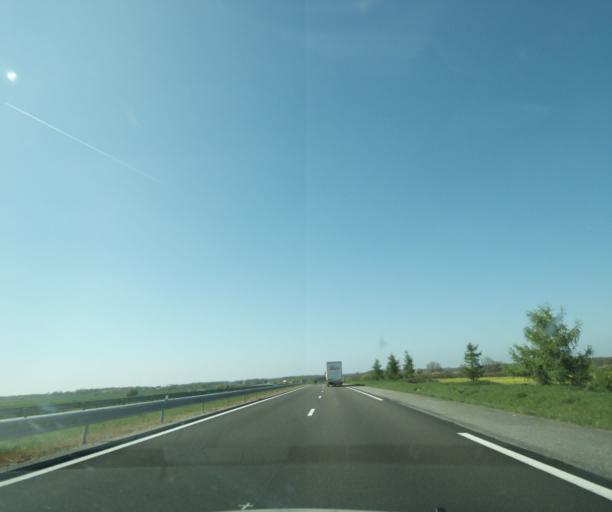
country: FR
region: Centre
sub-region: Departement du Loiret
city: Briare
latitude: 47.6311
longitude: 2.7858
